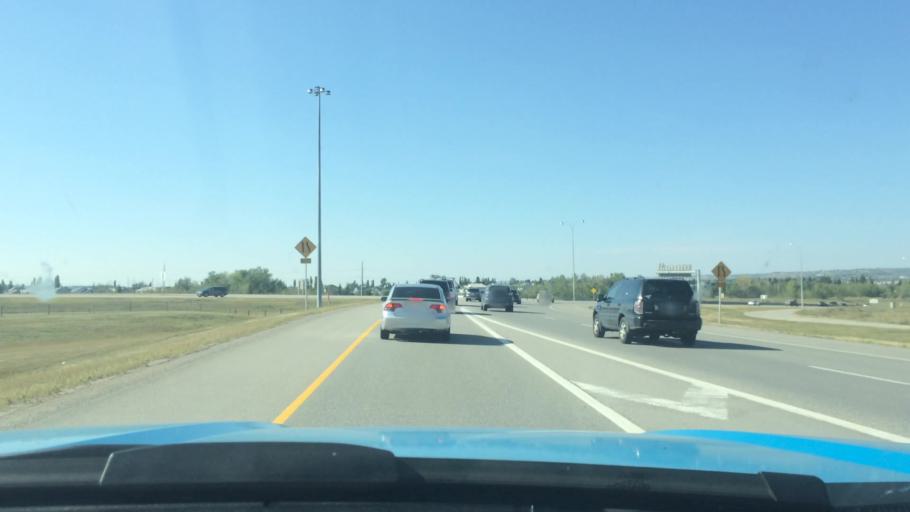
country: CA
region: Alberta
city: Calgary
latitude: 51.0902
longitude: -114.2312
